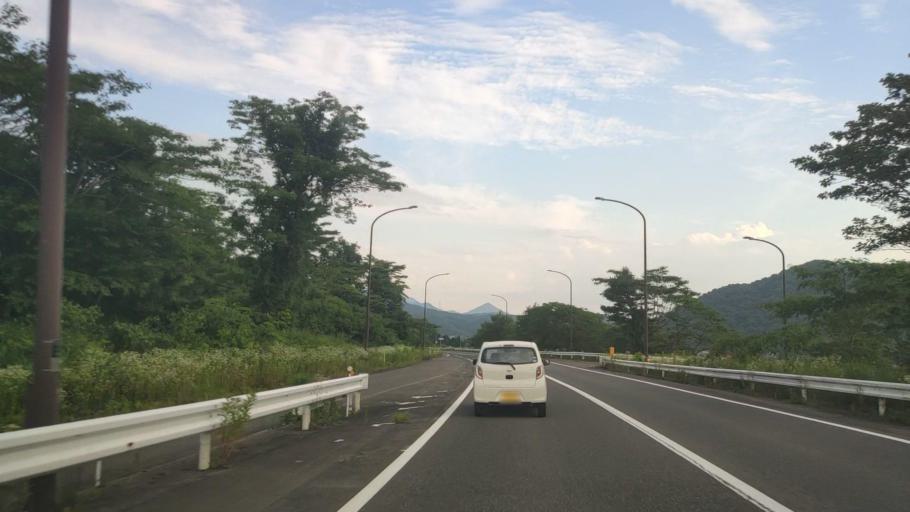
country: JP
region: Tottori
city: Kurayoshi
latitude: 35.2959
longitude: 133.7360
